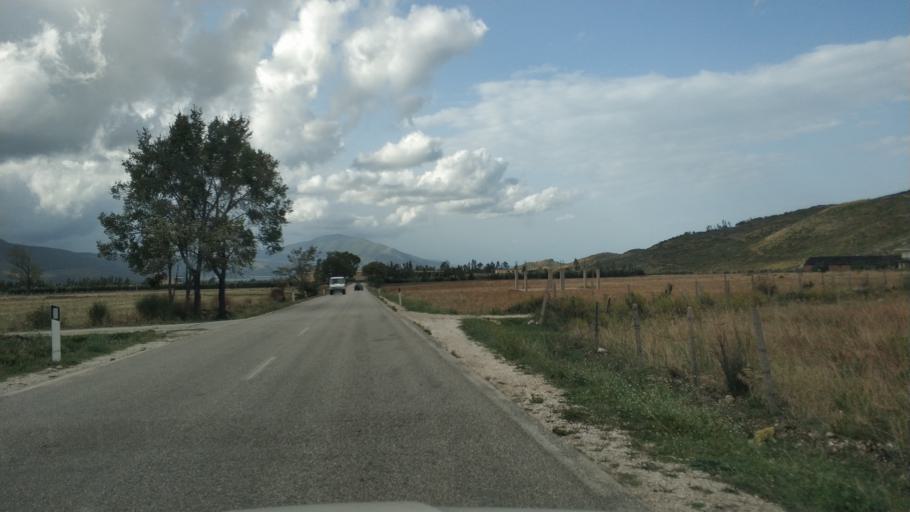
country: AL
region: Vlore
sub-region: Rrethi i Vlores
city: Orikum
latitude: 40.2759
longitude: 19.5073
